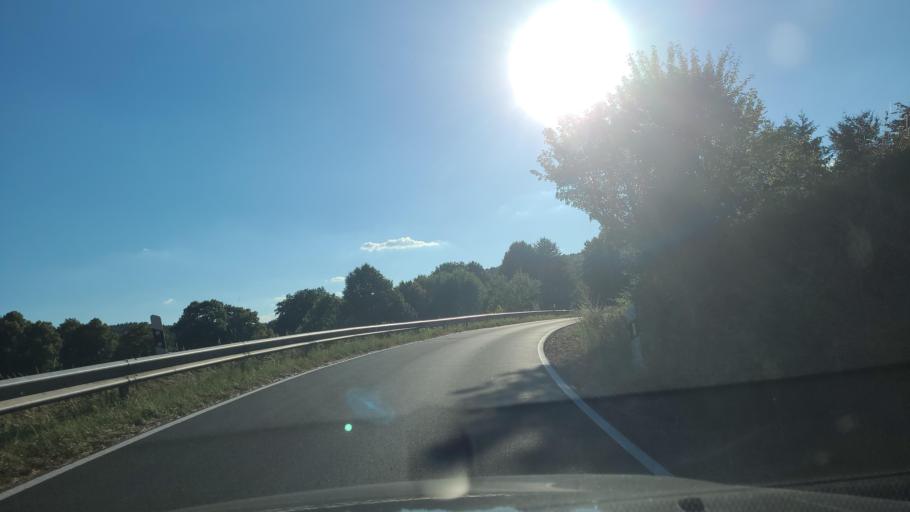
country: DE
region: Rheinland-Pfalz
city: Dierscheid
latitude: 49.9068
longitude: 6.7473
